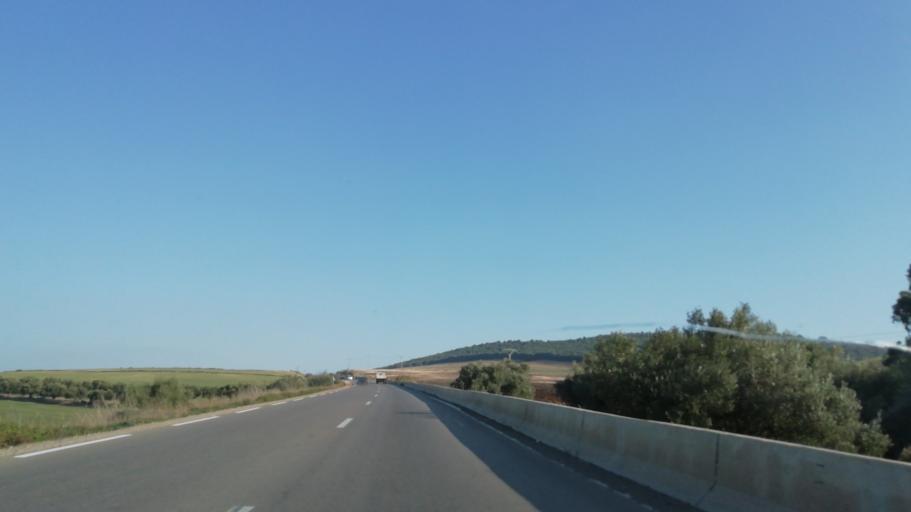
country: DZ
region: Ain Temouchent
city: Hammam Bou Hadjar
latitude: 35.1669
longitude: -0.8937
